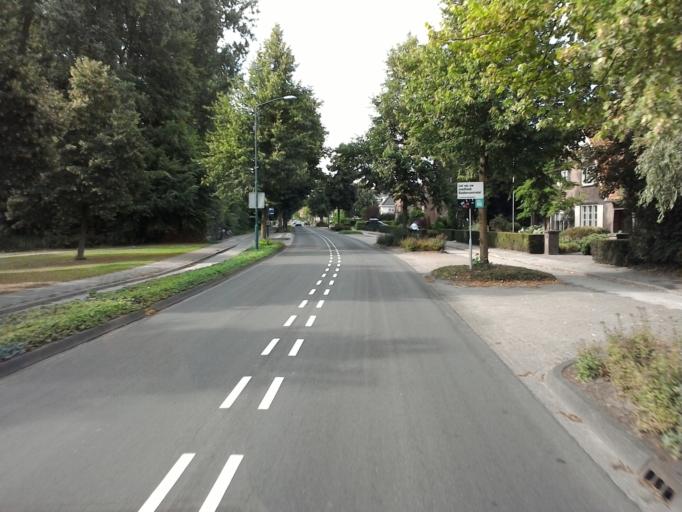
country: NL
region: North Brabant
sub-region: Gemeente Sint-Oedenrode
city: Sint-Oedenrode
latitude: 51.5660
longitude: 5.4657
